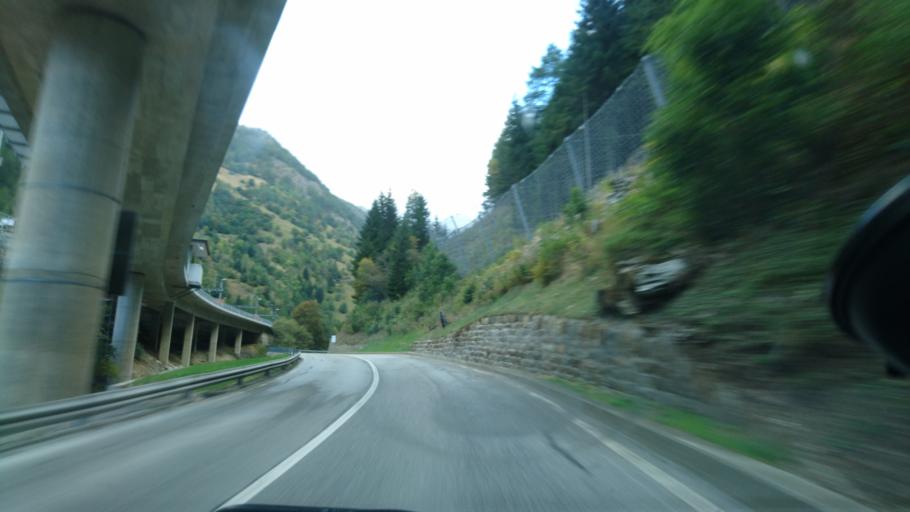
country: CH
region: Valais
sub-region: Leuk District
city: Gampel
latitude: 46.3658
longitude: 7.7567
